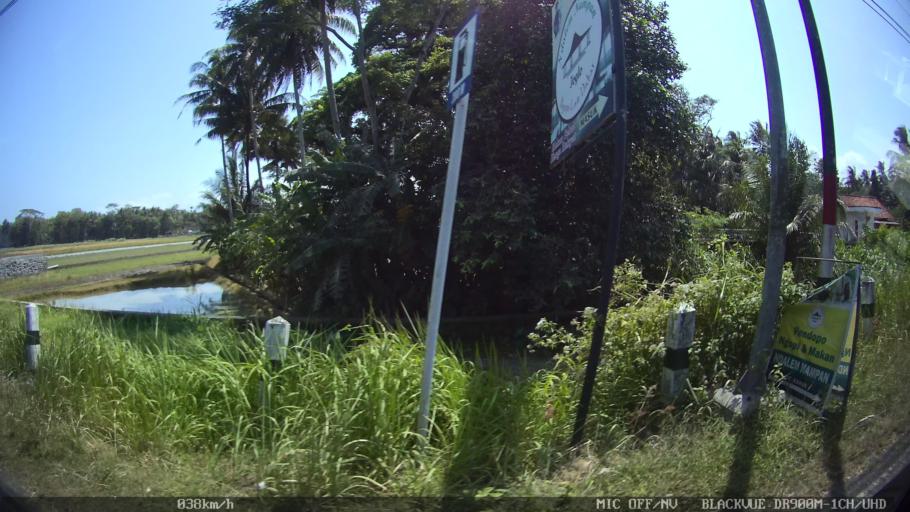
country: ID
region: Daerah Istimewa Yogyakarta
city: Srandakan
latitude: -7.9510
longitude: 110.2122
